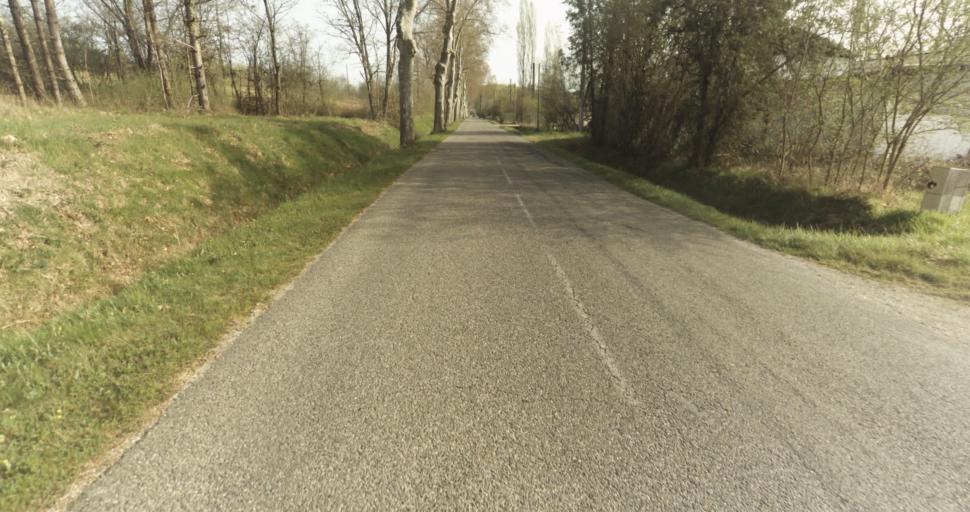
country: FR
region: Midi-Pyrenees
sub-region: Departement du Tarn-et-Garonne
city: Moissac
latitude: 44.1457
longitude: 1.1046
